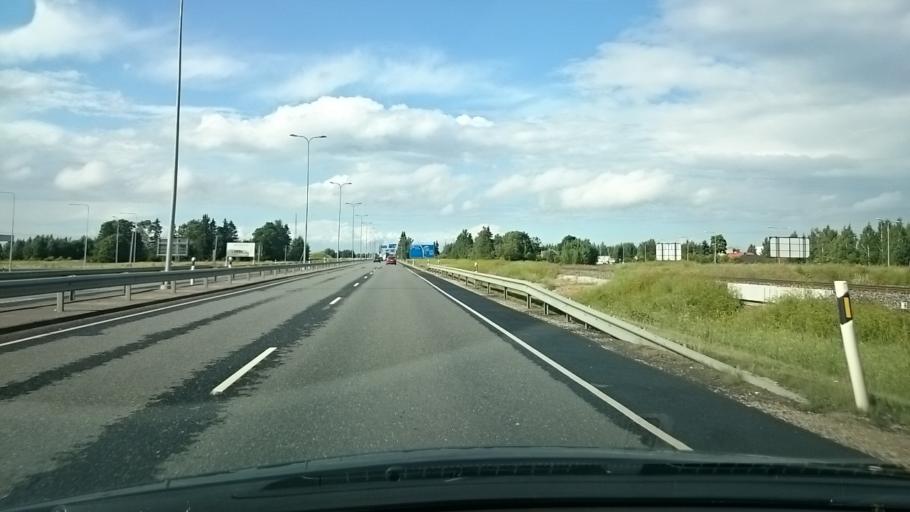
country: EE
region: Tartu
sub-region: UElenurme vald
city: Ulenurme
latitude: 58.3355
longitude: 26.7136
